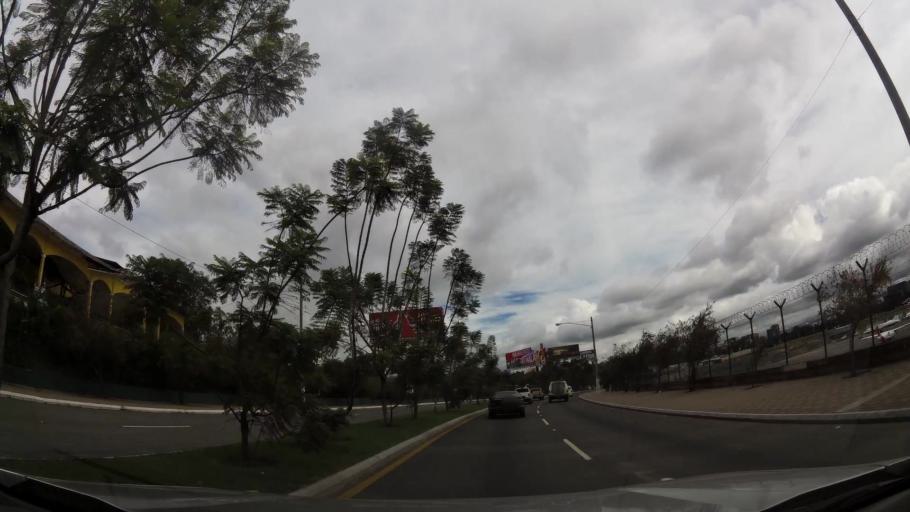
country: GT
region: Guatemala
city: Santa Catarina Pinula
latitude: 14.5924
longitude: -90.5300
